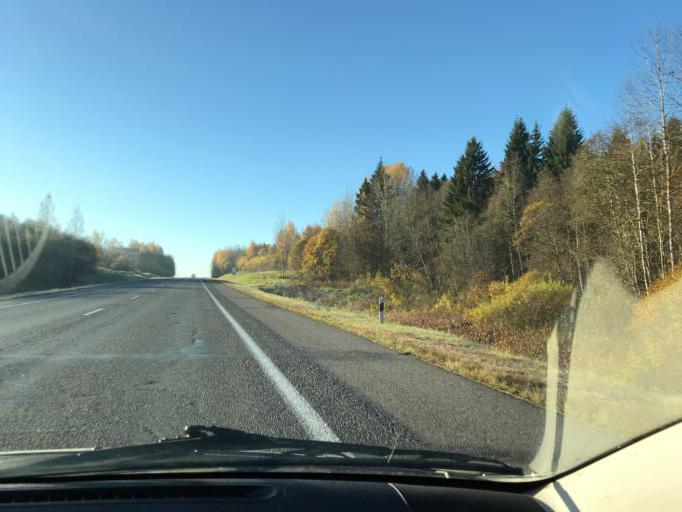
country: BY
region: Vitebsk
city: Vitebsk
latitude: 54.9172
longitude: 30.3751
